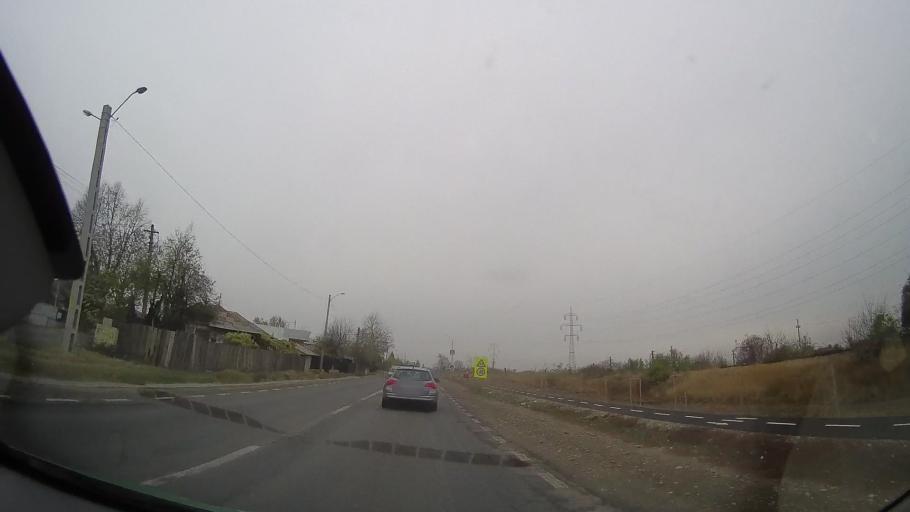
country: RO
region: Prahova
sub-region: Comuna Blejoiu
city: Ploiestiori
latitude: 44.9811
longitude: 26.0164
